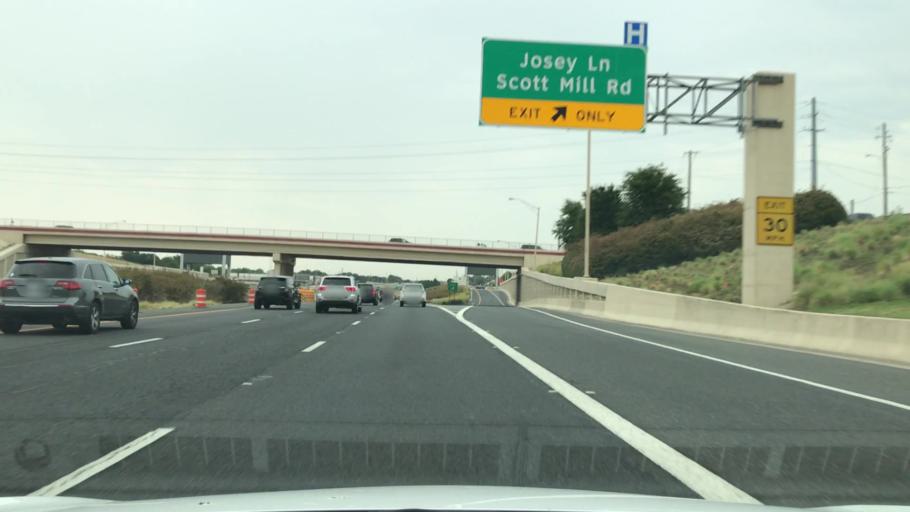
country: US
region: Texas
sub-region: Dallas County
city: Carrollton
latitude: 32.9842
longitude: -96.8986
